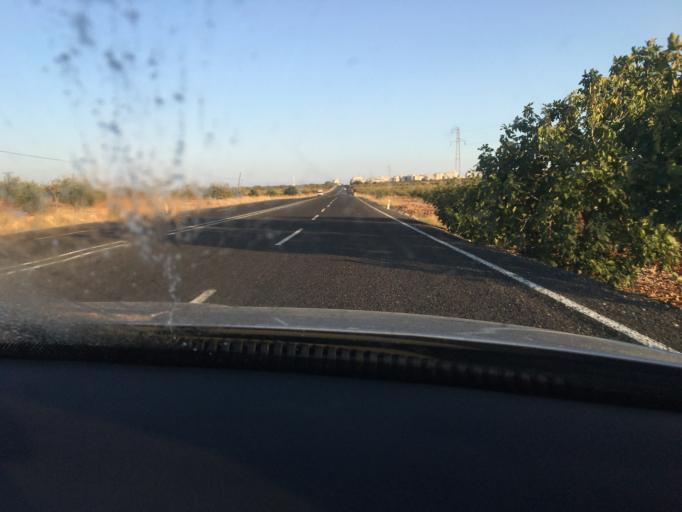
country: TR
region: Sanliurfa
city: Halfeti
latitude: 37.2368
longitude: 37.9251
